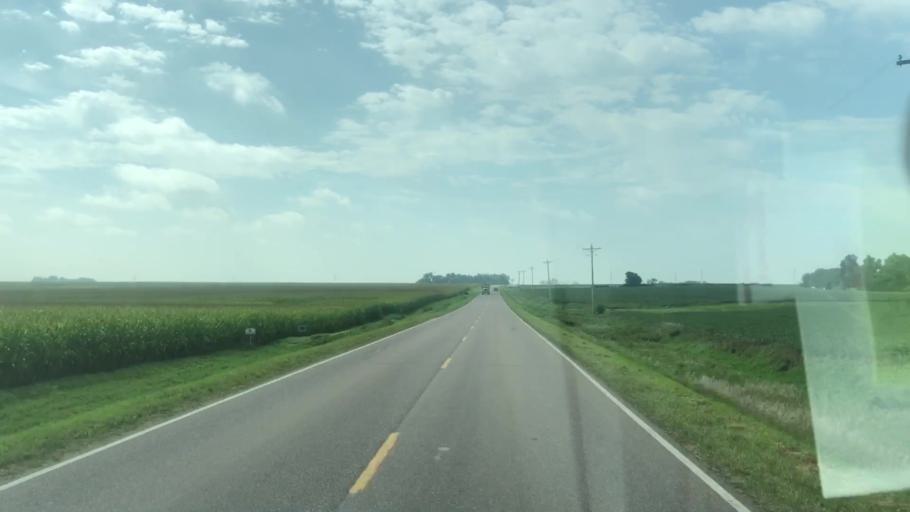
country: US
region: Iowa
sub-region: Lyon County
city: George
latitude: 43.2199
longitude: -96.0006
